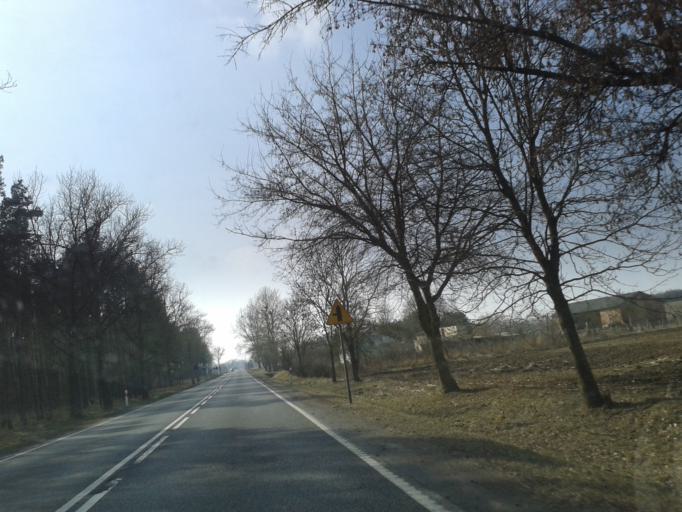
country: PL
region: Pomeranian Voivodeship
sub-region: Powiat czluchowski
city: Debrzno
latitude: 53.5762
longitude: 17.0976
